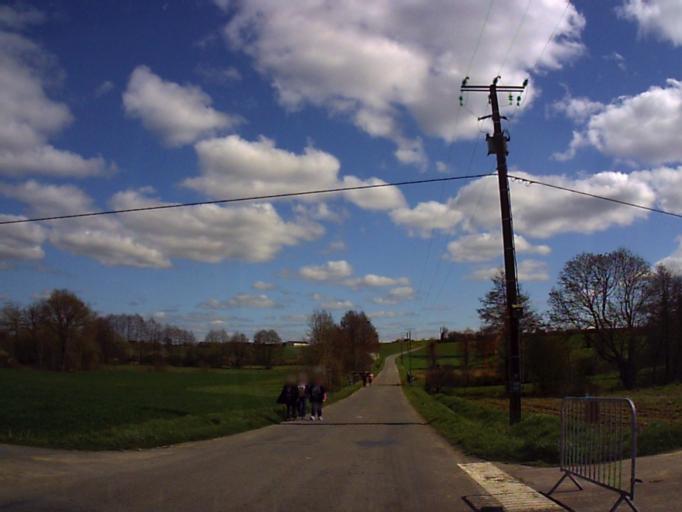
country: FR
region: Brittany
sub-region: Departement d'Ille-et-Vilaine
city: Boisgervilly
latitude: 48.1044
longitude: -2.1216
